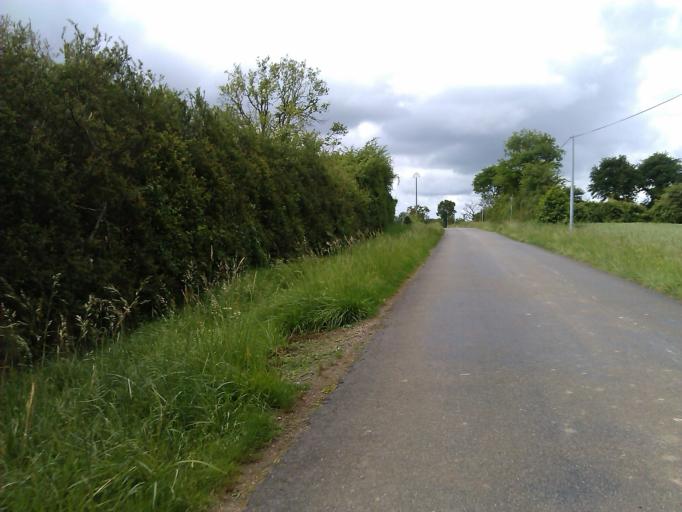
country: FR
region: Poitou-Charentes
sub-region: Departement de la Vienne
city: Charroux
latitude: 46.0960
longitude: 0.5109
